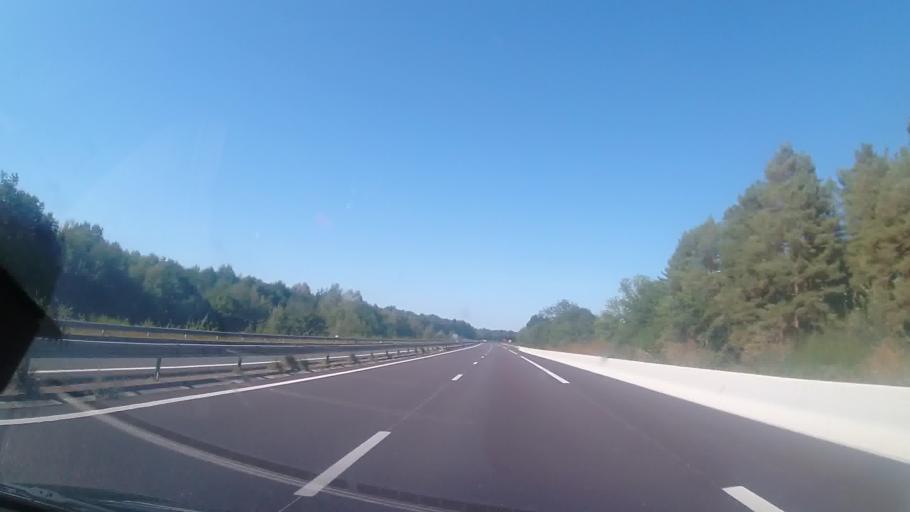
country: FR
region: Centre
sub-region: Departement du Loir-et-Cher
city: Nouan-le-Fuzelier
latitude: 47.5173
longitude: 2.0077
